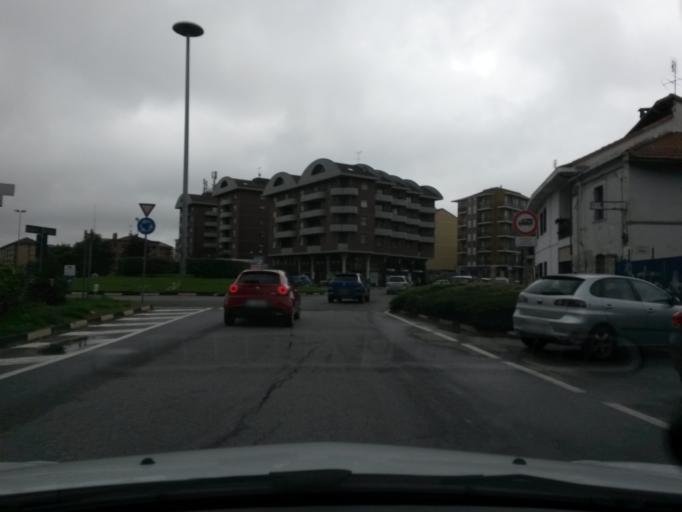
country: IT
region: Piedmont
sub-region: Provincia di Torino
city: Rivoli
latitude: 45.0759
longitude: 7.5192
